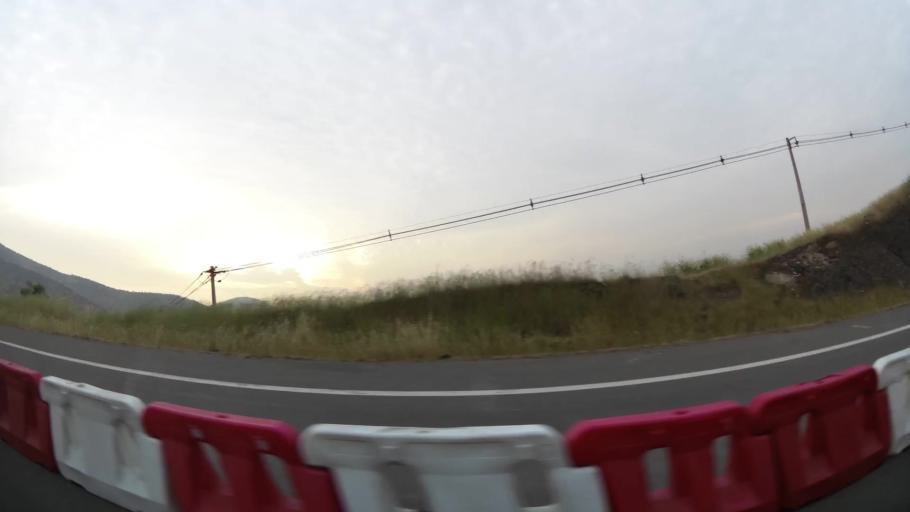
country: CL
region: Santiago Metropolitan
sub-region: Provincia de Chacabuco
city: Chicureo Abajo
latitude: -33.3296
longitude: -70.6278
